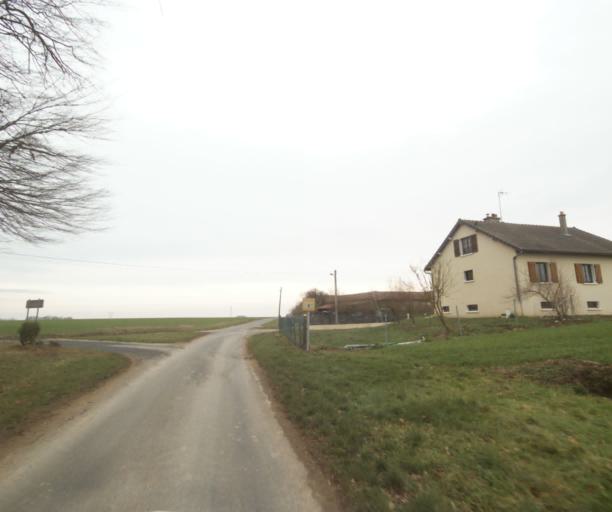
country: FR
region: Champagne-Ardenne
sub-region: Departement de la Haute-Marne
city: Villiers-en-Lieu
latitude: 48.6342
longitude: 4.8126
